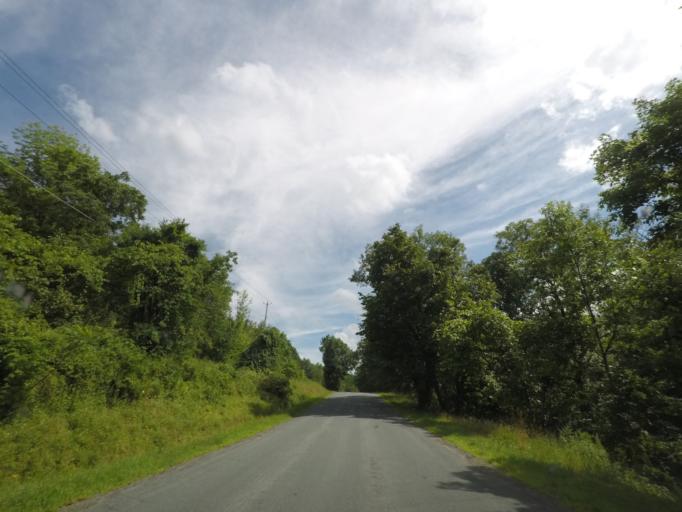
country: US
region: New York
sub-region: Rensselaer County
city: Poestenkill
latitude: 42.6759
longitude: -73.5513
